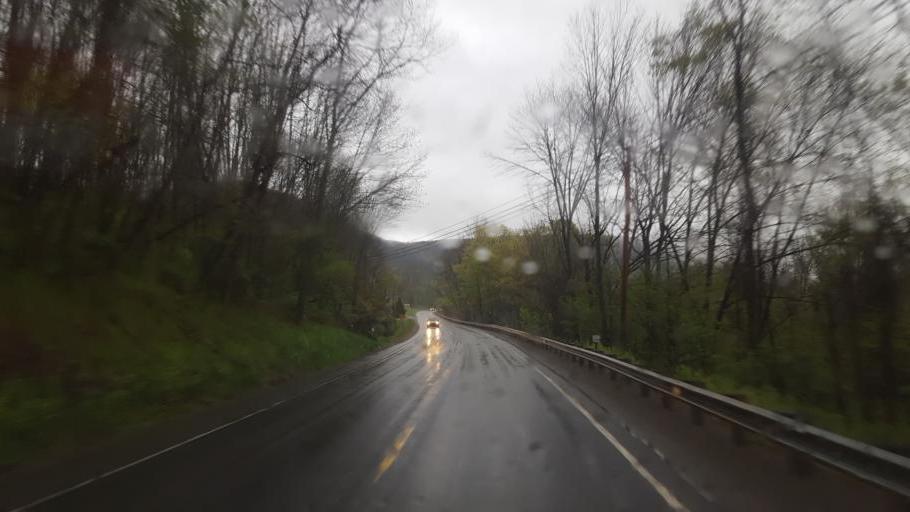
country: US
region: Pennsylvania
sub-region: Tioga County
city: Westfield
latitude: 41.9480
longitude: -77.4706
